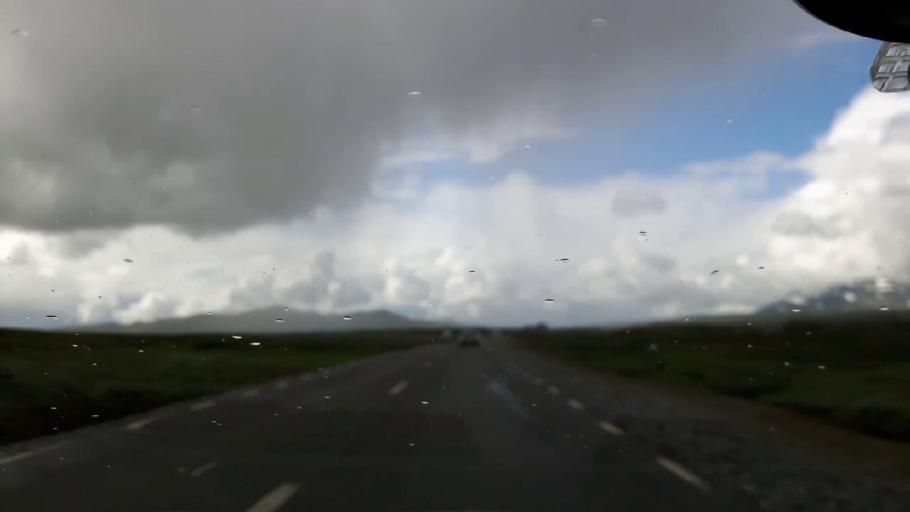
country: NO
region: Nordland
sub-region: Hattfjelldal
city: Hattfjelldal
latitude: 65.1050
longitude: 14.4735
